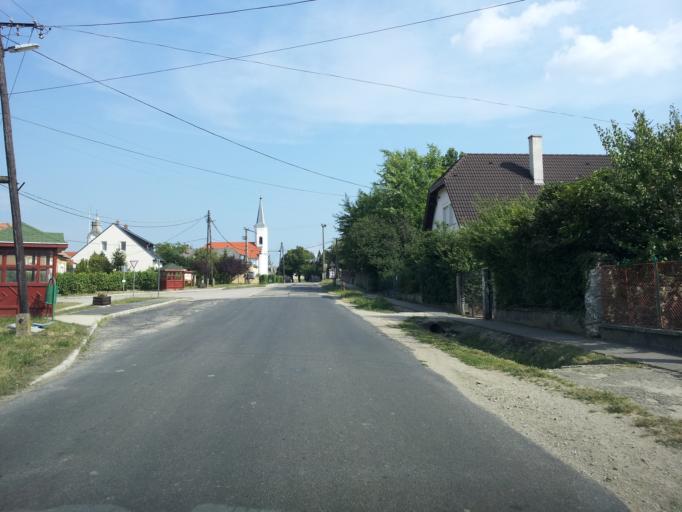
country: HU
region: Veszprem
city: Nemesvamos
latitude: 47.0565
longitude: 17.8694
